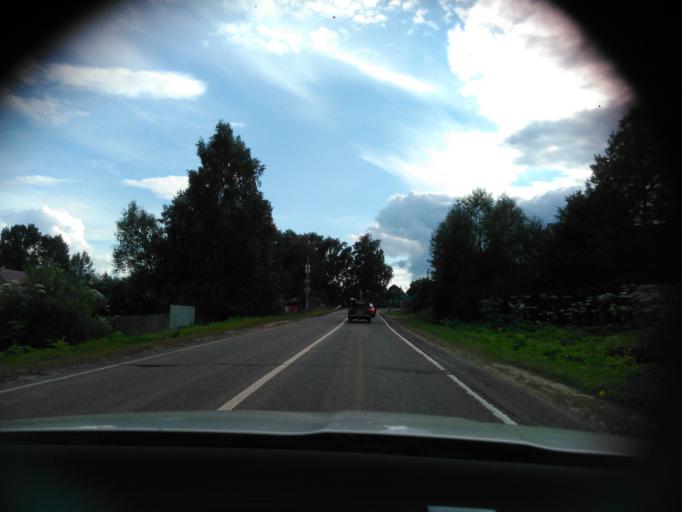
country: RU
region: Moskovskaya
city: Klin
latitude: 56.1550
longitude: 36.7531
